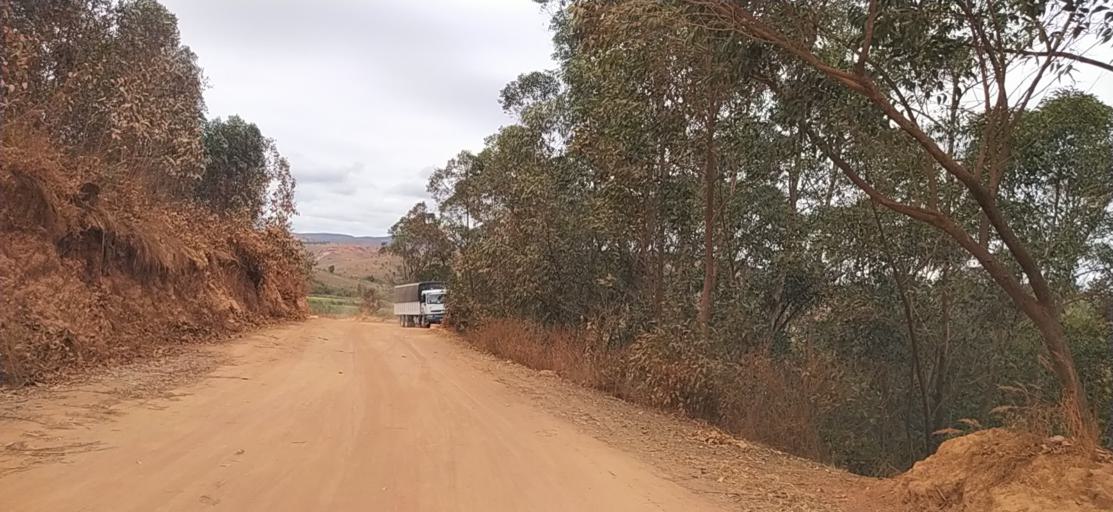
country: MG
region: Alaotra Mangoro
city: Ambatondrazaka
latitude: -18.0057
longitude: 48.2614
